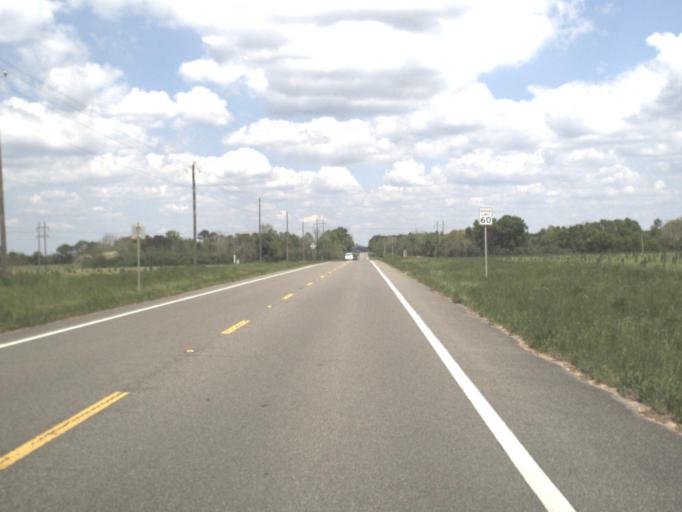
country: US
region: Florida
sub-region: Okaloosa County
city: Crestview
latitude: 30.8072
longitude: -86.6793
